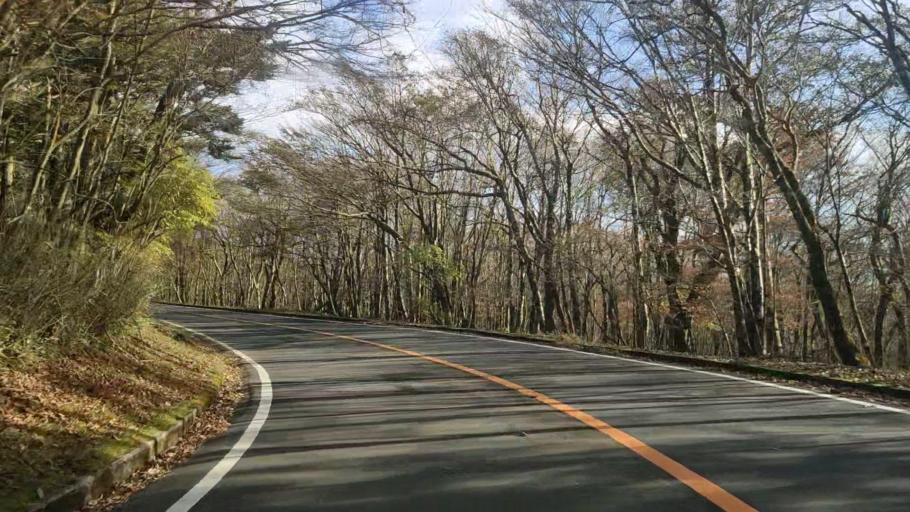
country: JP
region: Shizuoka
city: Fuji
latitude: 35.3016
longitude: 138.7532
